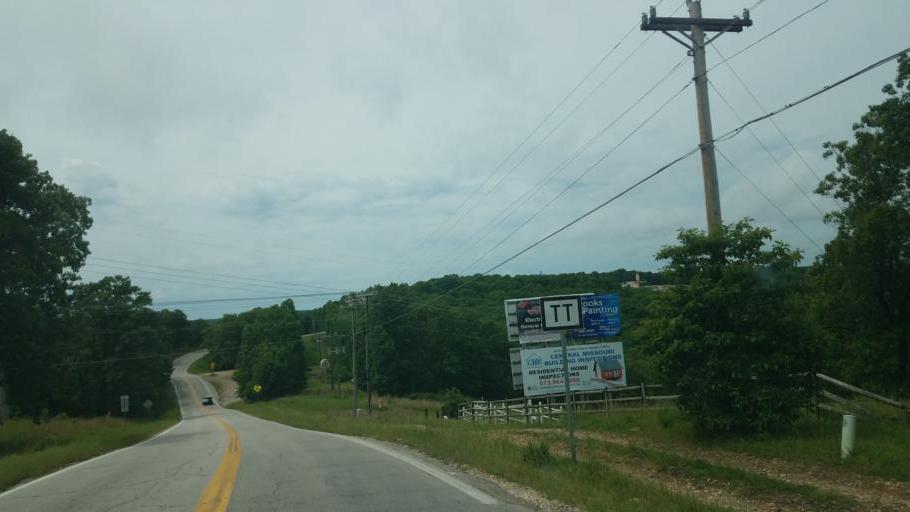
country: US
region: Missouri
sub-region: Camden County
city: Four Seasons
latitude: 38.1584
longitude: -92.7446
